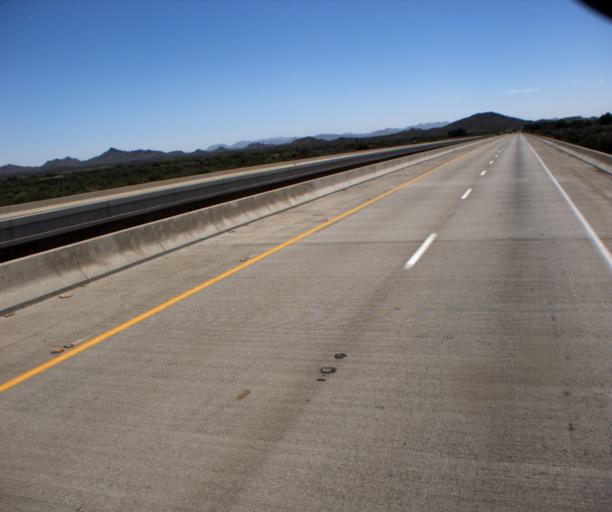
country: US
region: Arizona
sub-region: Maricopa County
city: Buckeye
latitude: 33.3359
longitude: -112.6237
